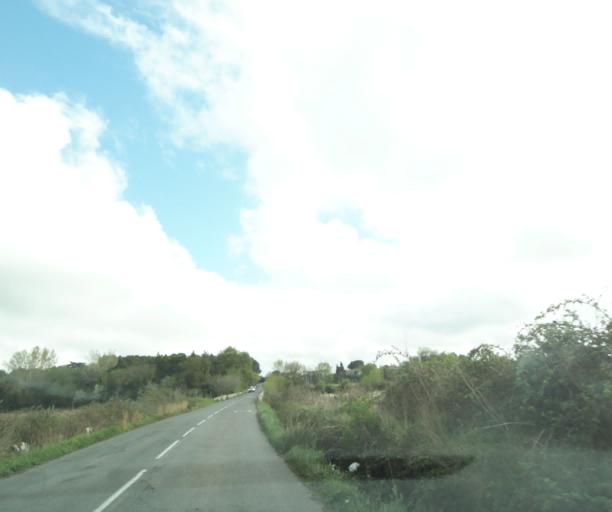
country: FR
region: Languedoc-Roussillon
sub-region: Departement de l'Herault
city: Saussan
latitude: 43.5757
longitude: 3.7710
